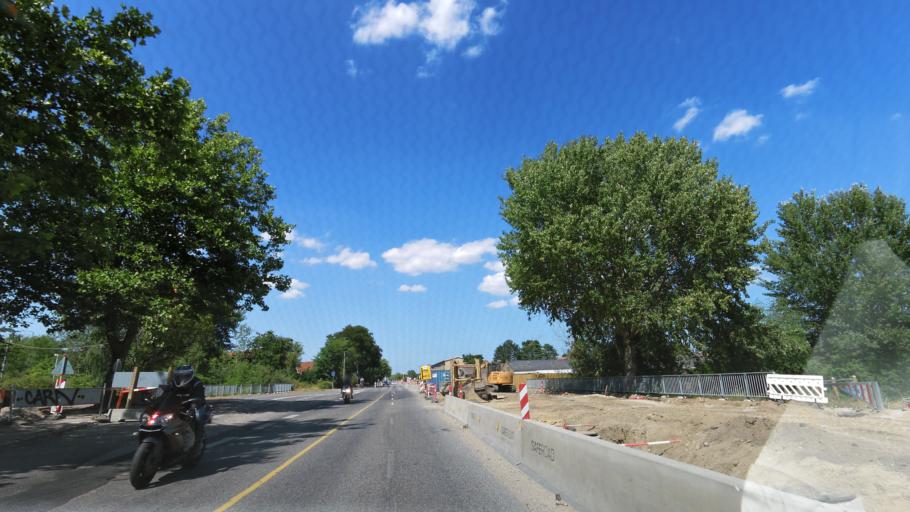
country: DK
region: South Denmark
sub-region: Odense Kommune
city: Odense
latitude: 55.4031
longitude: 10.3400
